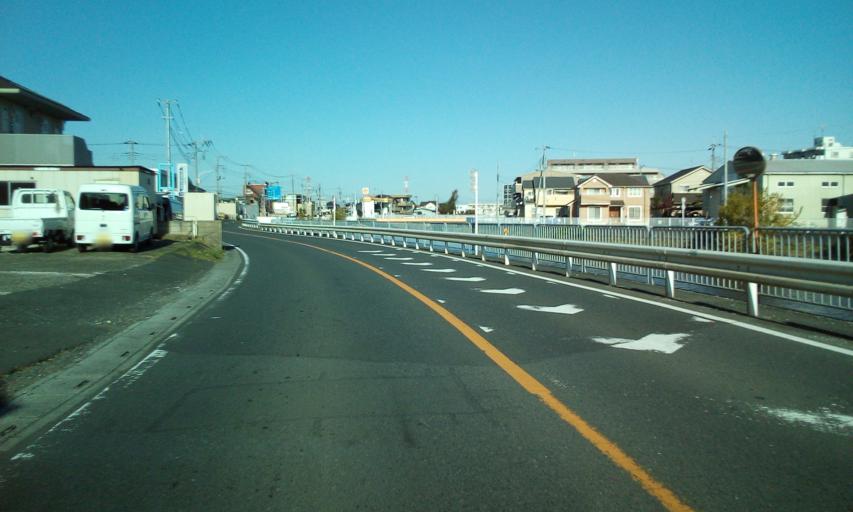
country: JP
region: Chiba
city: Nagareyama
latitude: 35.8396
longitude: 139.8838
